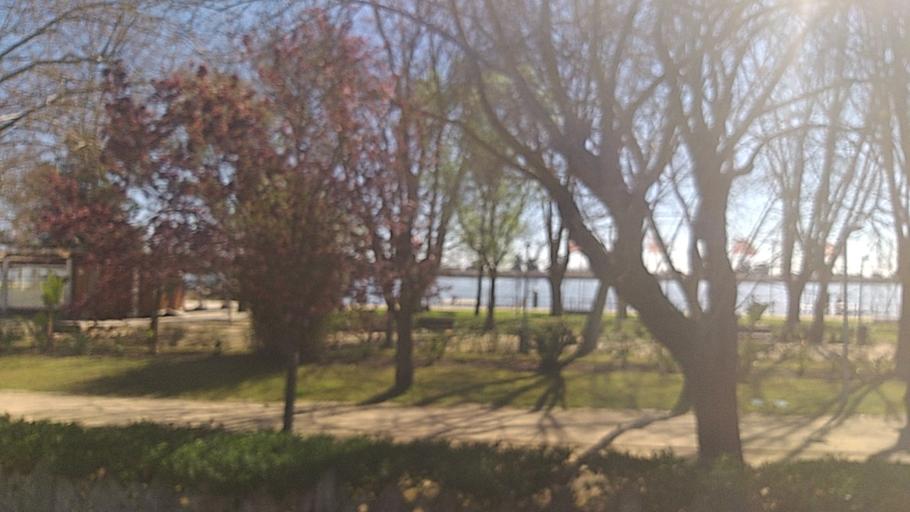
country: PT
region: Lisbon
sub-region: Vila Franca de Xira
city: Vila Franca de Xira
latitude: 38.9547
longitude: -8.9863
